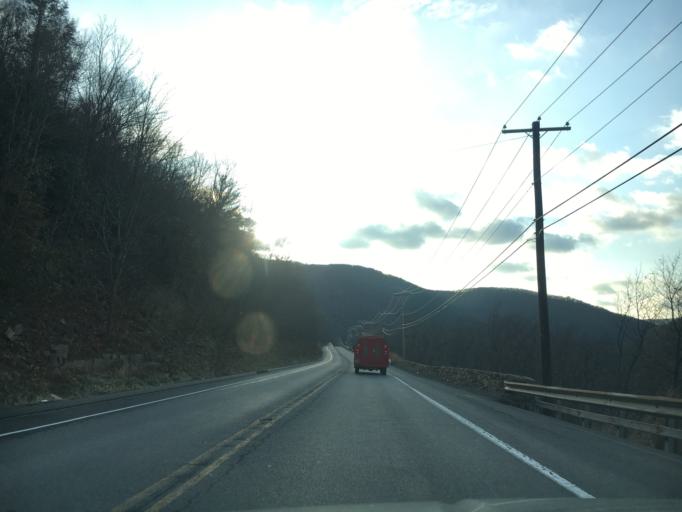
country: US
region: Pennsylvania
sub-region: Carbon County
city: Jim Thorpe
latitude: 40.8623
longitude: -75.7240
